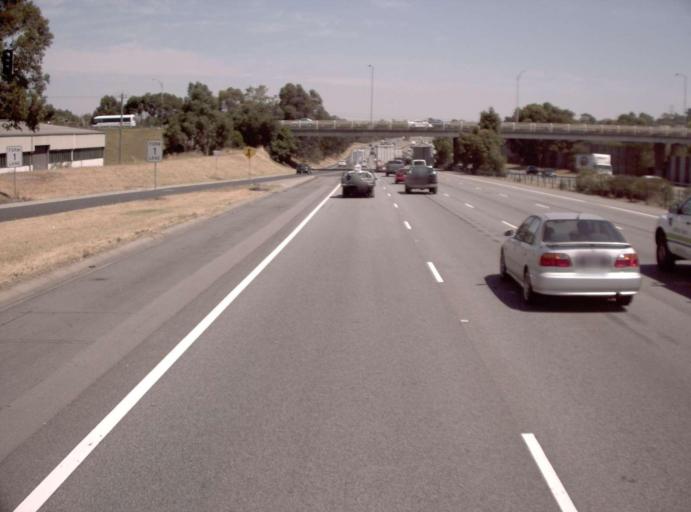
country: AU
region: Victoria
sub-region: Monash
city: Notting Hill
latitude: -37.8926
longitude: 145.1275
